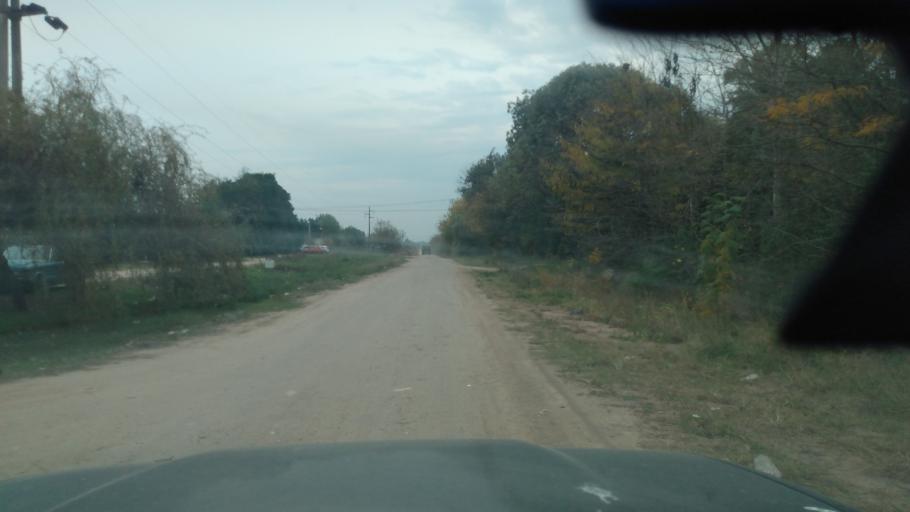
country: AR
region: Buenos Aires
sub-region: Partido de Lujan
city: Lujan
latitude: -34.5599
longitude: -59.1451
